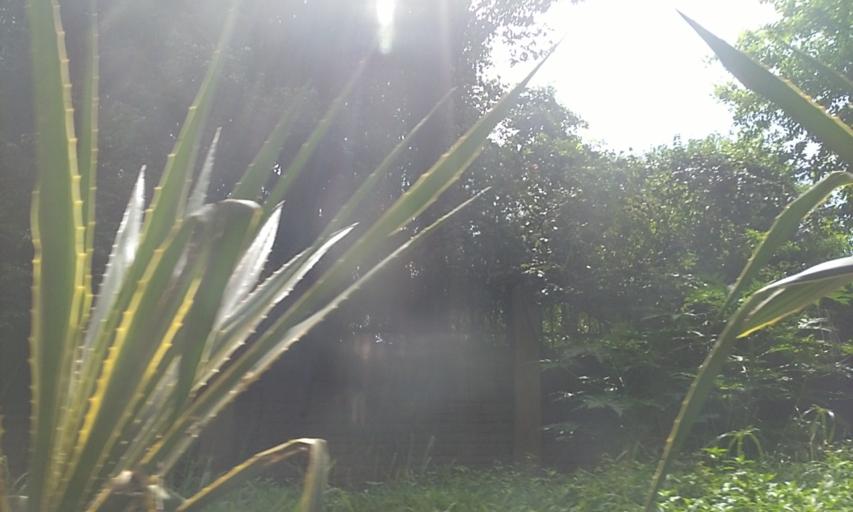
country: UG
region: Central Region
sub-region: Kampala District
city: Kampala
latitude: 0.3302
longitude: 32.5981
